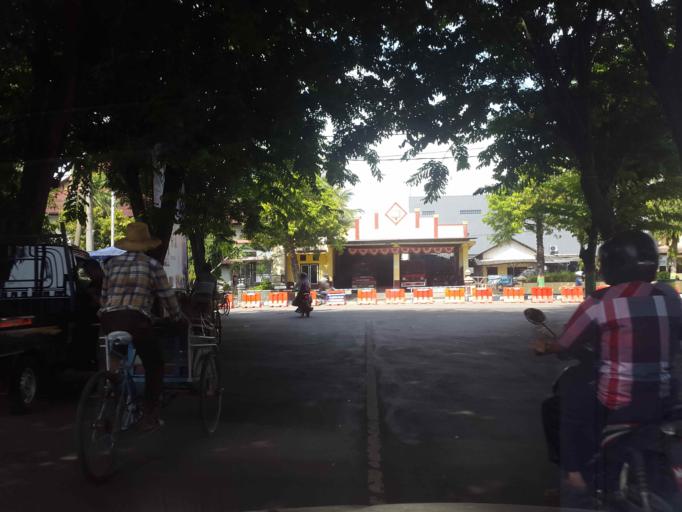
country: ID
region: East Java
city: Sumenep
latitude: -7.0089
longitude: 113.8599
